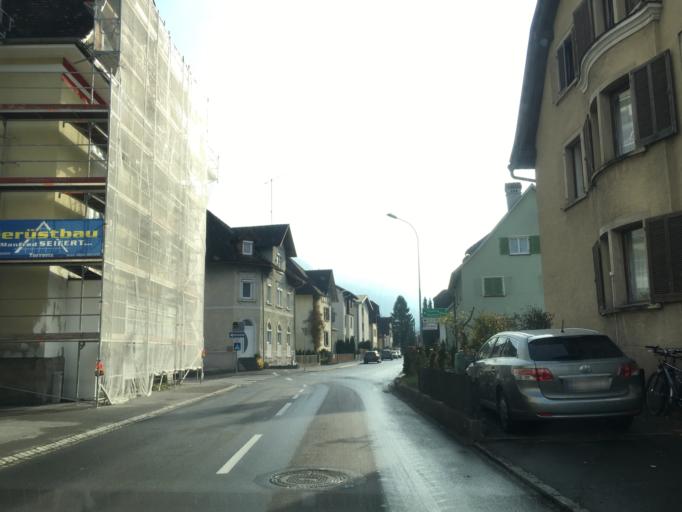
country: AT
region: Vorarlberg
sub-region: Politischer Bezirk Bludenz
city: Bludenz
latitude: 47.1527
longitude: 9.8193
